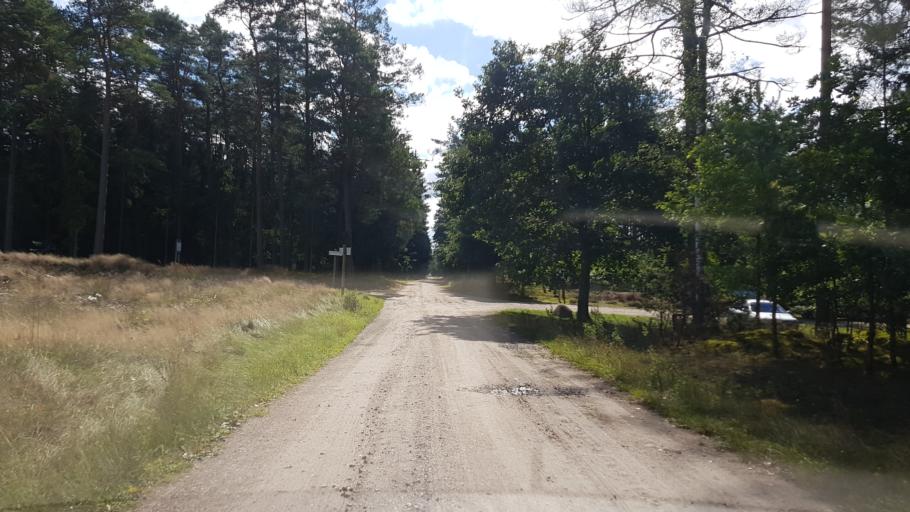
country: PL
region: West Pomeranian Voivodeship
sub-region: Powiat bialogardzki
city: Tychowo
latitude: 54.0193
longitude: 16.2988
